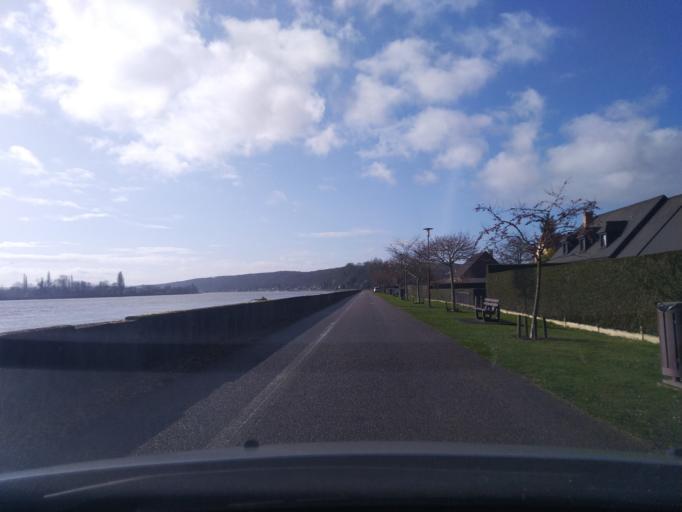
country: FR
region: Haute-Normandie
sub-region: Departement de la Seine-Maritime
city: Duclair
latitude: 49.4723
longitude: 0.8633
